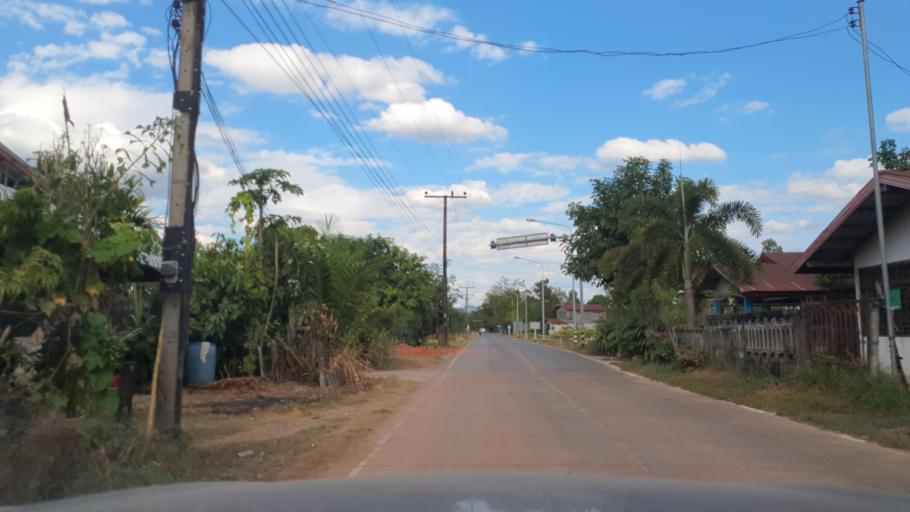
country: TH
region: Nakhon Phanom
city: Ban Phaeng
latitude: 17.9922
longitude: 104.1585
